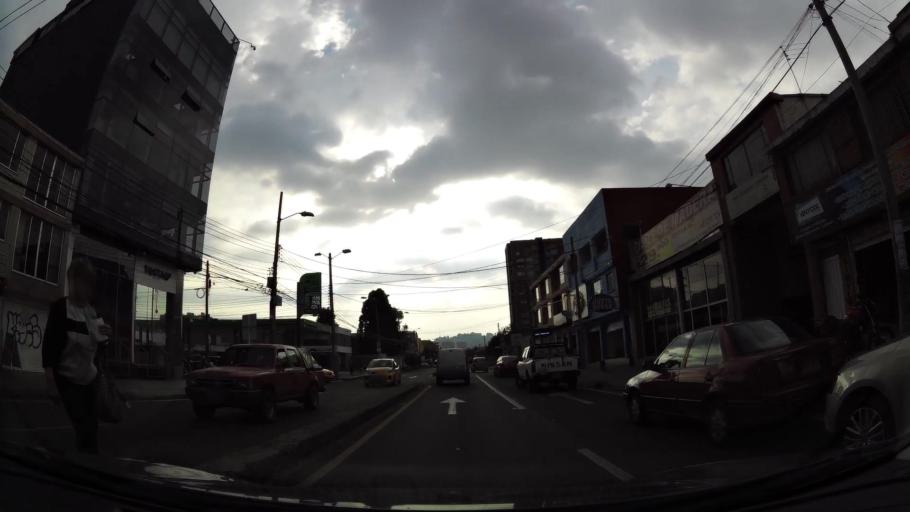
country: CO
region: Bogota D.C.
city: Barrio San Luis
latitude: 4.7163
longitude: -74.0599
